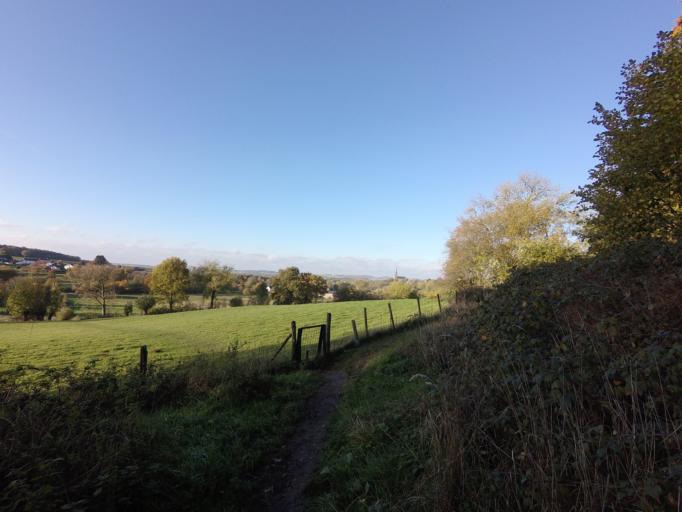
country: BE
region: Wallonia
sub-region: Province de Liege
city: Plombieres
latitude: 50.7778
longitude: 5.9627
